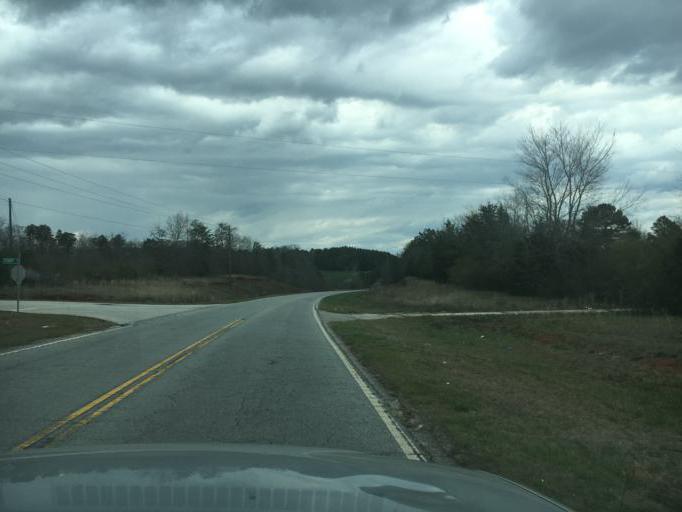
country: US
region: South Carolina
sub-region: Oconee County
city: Walhalla
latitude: 34.7257
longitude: -83.0561
